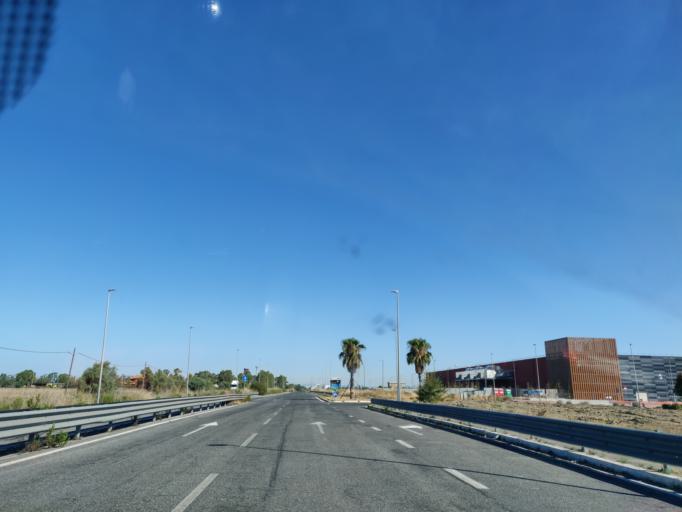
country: IT
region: Latium
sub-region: Citta metropolitana di Roma Capitale
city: Npp 23 (Parco Leonardo)
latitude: 41.8045
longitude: 12.2945
